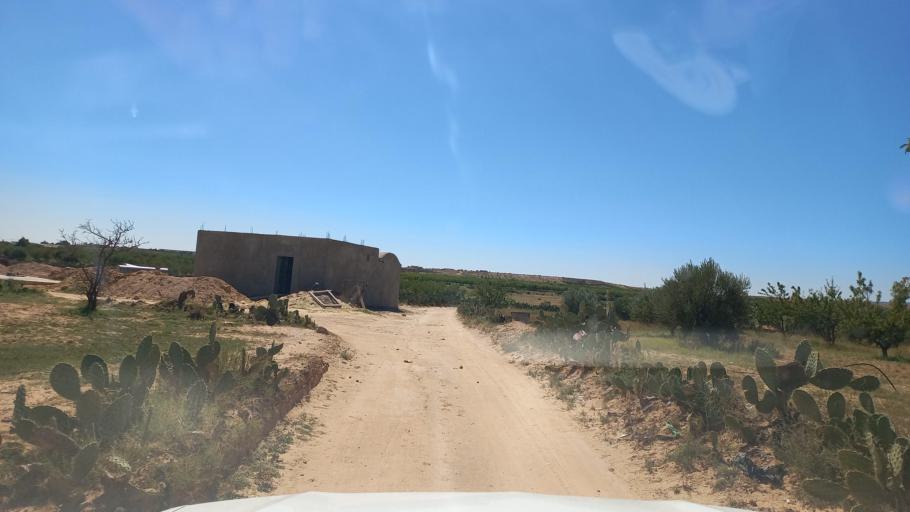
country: TN
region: Al Qasrayn
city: Sbiba
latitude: 35.3598
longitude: 9.0863
